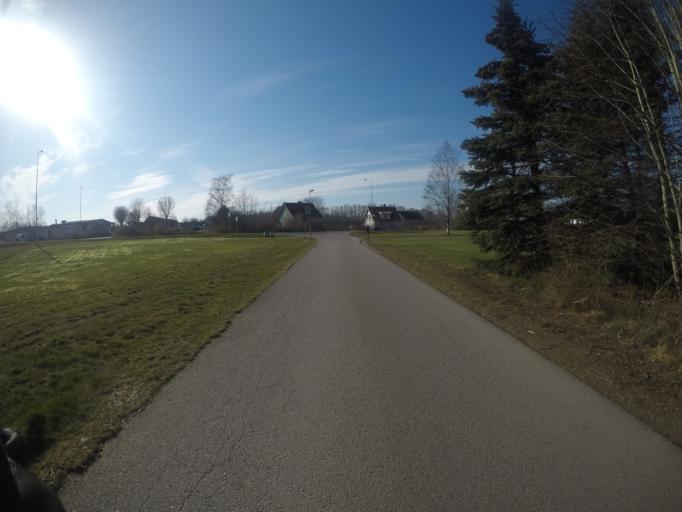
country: SE
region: Halland
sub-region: Laholms Kommun
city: Laholm
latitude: 56.5035
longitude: 13.0628
